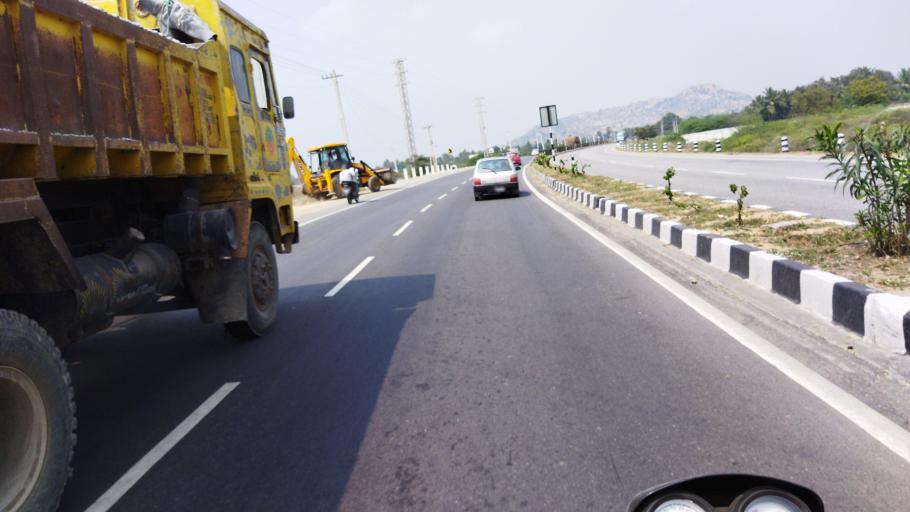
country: IN
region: Telangana
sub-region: Nalgonda
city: Nalgonda
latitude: 17.0803
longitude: 79.2777
